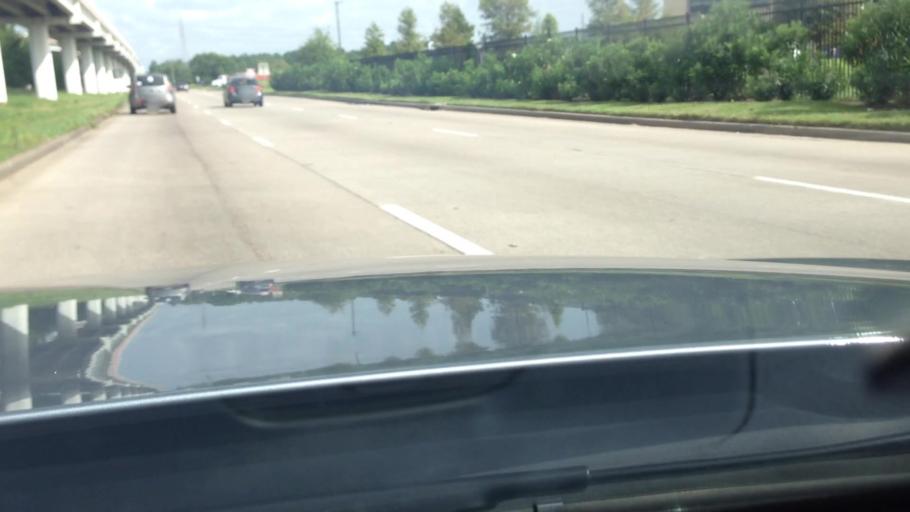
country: US
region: Texas
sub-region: Harris County
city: Hudson
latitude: 29.9379
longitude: -95.5168
